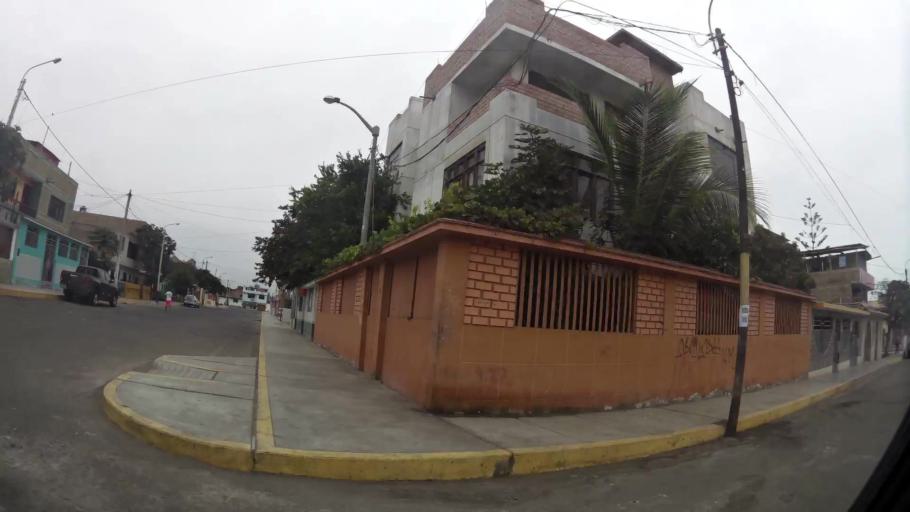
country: PE
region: Ancash
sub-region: Provincia de Santa
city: Chimbote
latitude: -9.0710
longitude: -78.5979
